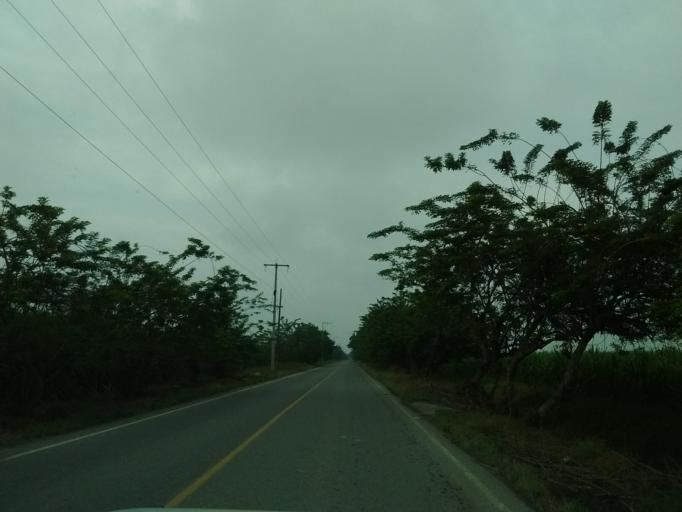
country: CO
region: Cauca
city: Padilla
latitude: 3.2276
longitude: -76.3399
